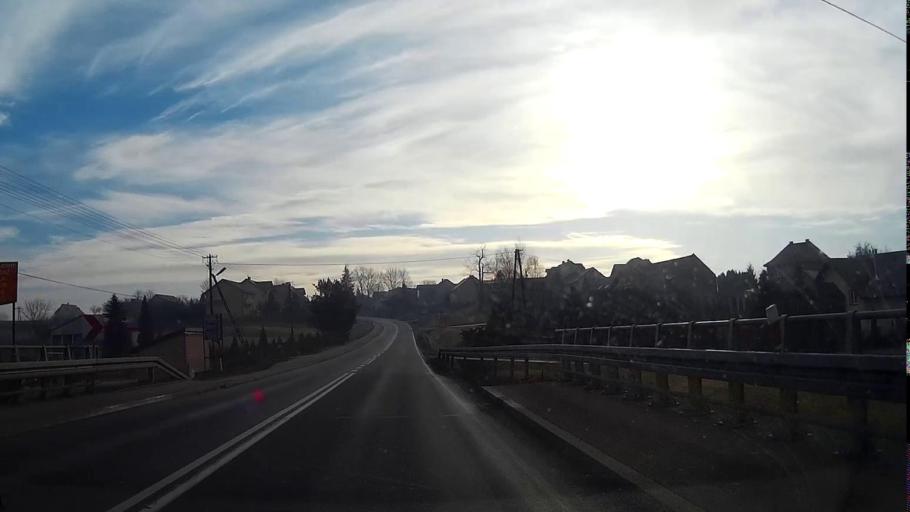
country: PL
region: Lesser Poland Voivodeship
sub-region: Powiat krakowski
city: Kaszow
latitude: 50.0393
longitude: 19.7395
